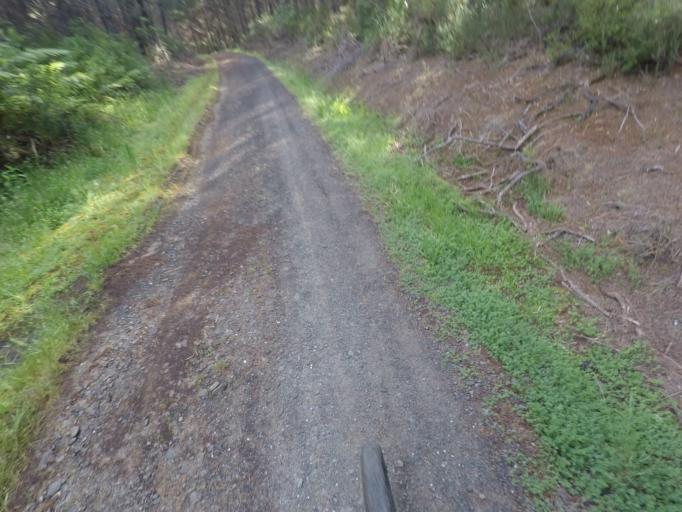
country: NZ
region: Auckland
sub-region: Auckland
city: Parakai
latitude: -36.7102
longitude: 174.5778
